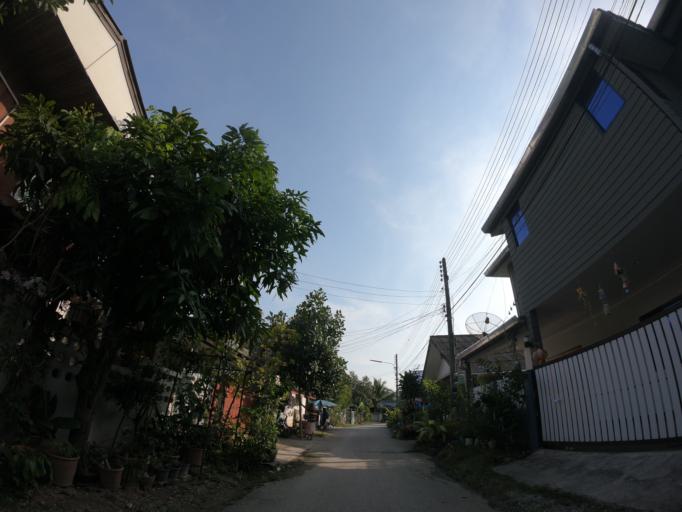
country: TH
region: Chiang Mai
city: Chiang Mai
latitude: 18.8290
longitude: 98.9904
